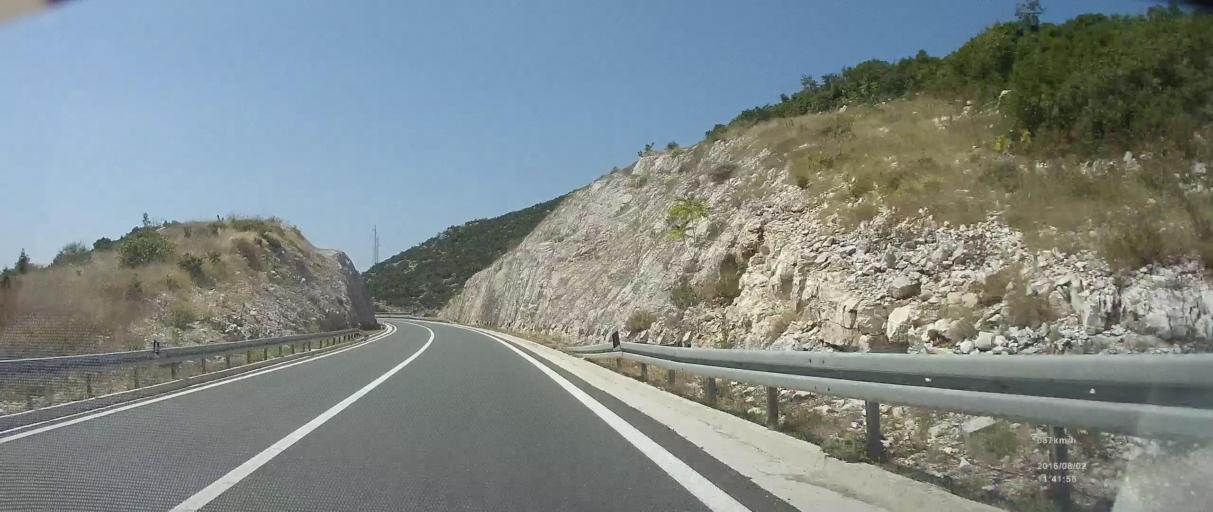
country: HR
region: Dubrovacko-Neretvanska
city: Komin
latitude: 43.0584
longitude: 17.4911
